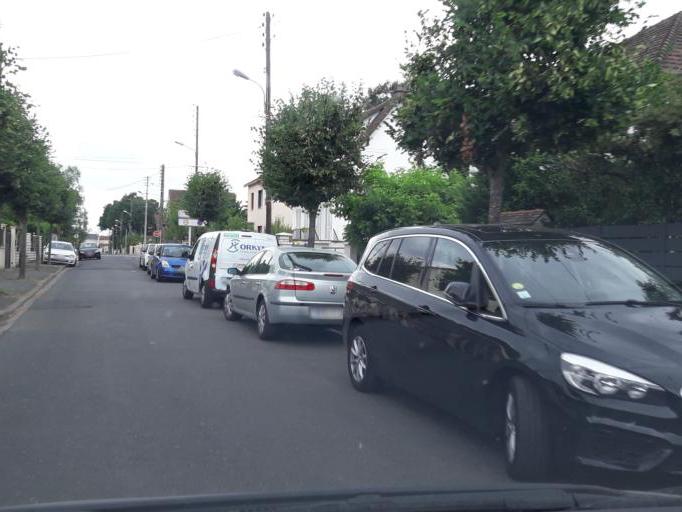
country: FR
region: Ile-de-France
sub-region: Departement de l'Essonne
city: Morsang-sur-Orge
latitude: 48.6509
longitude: 2.3605
